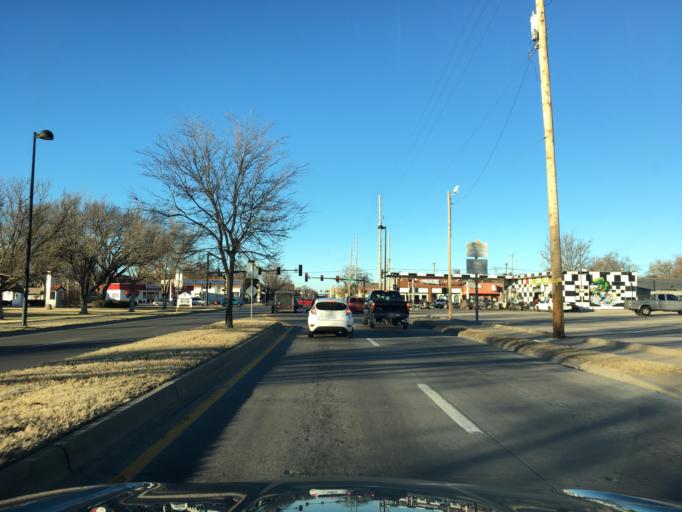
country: US
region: Kansas
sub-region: Sedgwick County
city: Wichita
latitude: 37.6794
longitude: -97.3530
